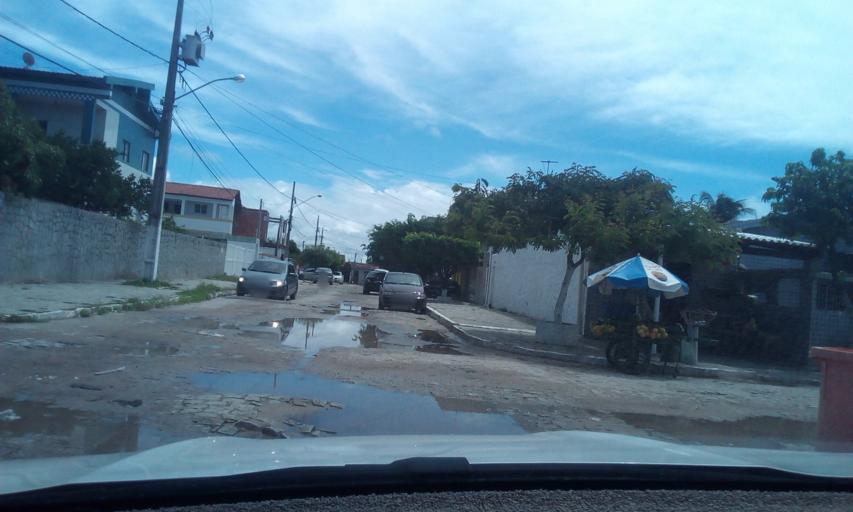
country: BR
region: Paraiba
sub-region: Cabedelo
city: Cabedelo
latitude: -6.9868
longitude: -34.8312
